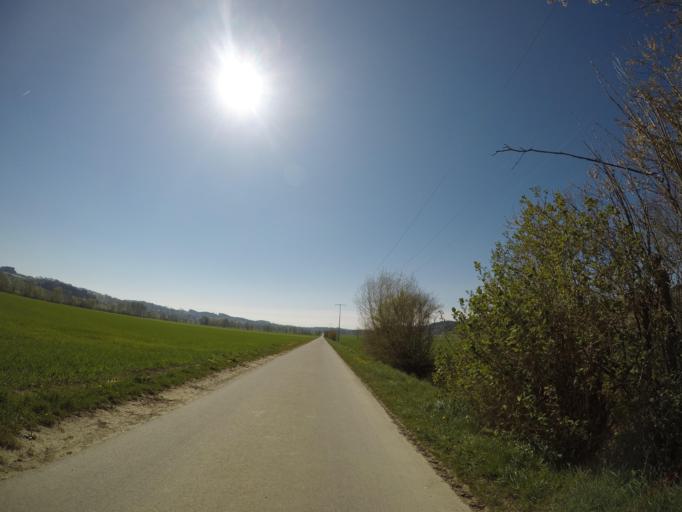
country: DE
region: Baden-Wuerttemberg
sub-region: Tuebingen Region
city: Wilhelmsdorf
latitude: 47.8430
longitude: 9.4417
